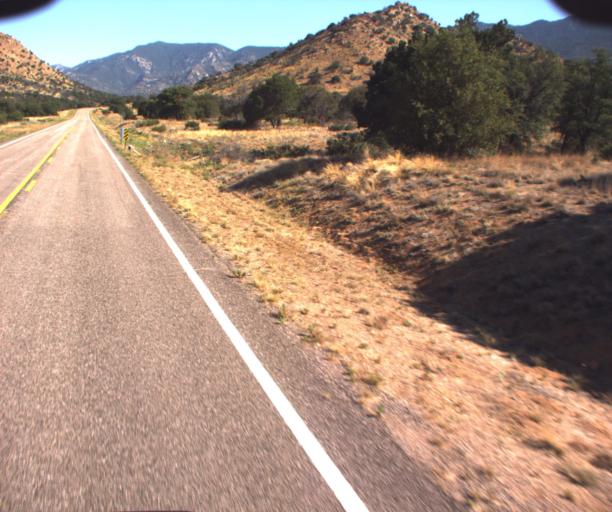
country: US
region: Arizona
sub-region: Graham County
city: Swift Trail Junction
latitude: 32.5805
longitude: -109.8508
